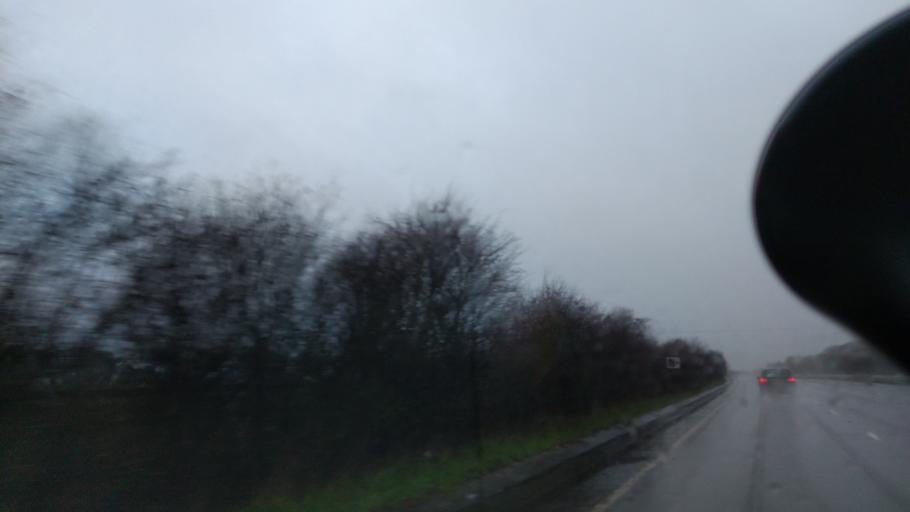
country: GB
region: England
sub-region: West Sussex
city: Rustington
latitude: 50.8397
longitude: -0.4674
